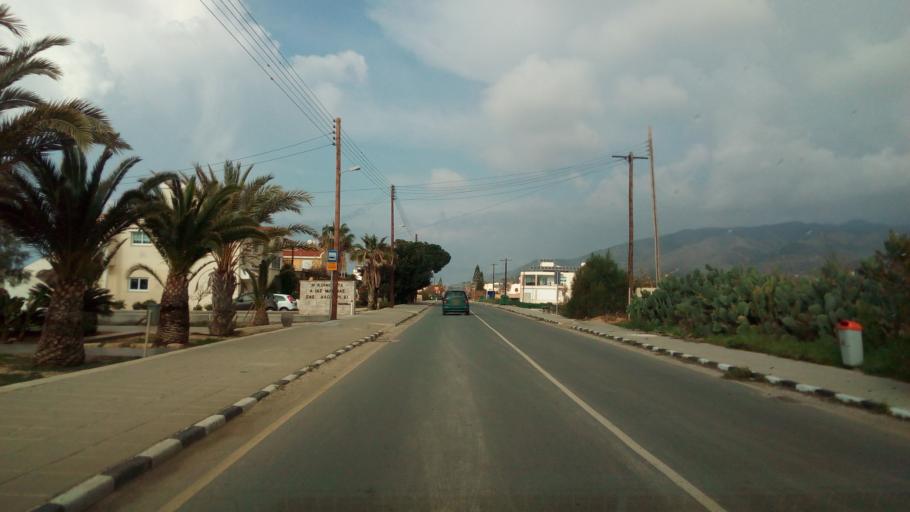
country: CY
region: Pafos
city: Polis
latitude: 35.1065
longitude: 32.5047
